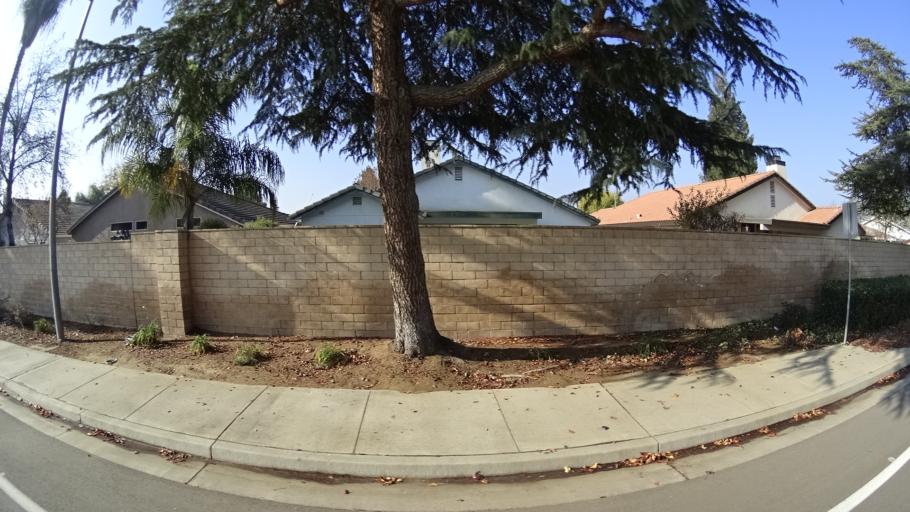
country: US
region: California
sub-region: Kern County
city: Greenacres
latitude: 35.3895
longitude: -119.1014
